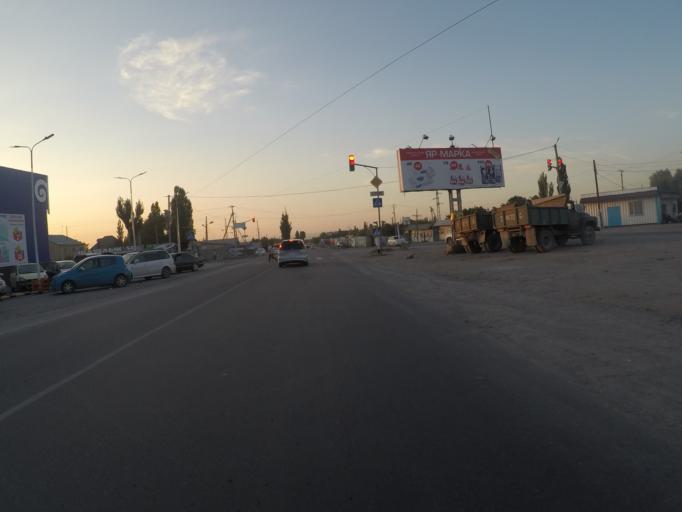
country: KG
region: Chuy
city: Lebedinovka
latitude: 42.8028
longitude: 74.6487
